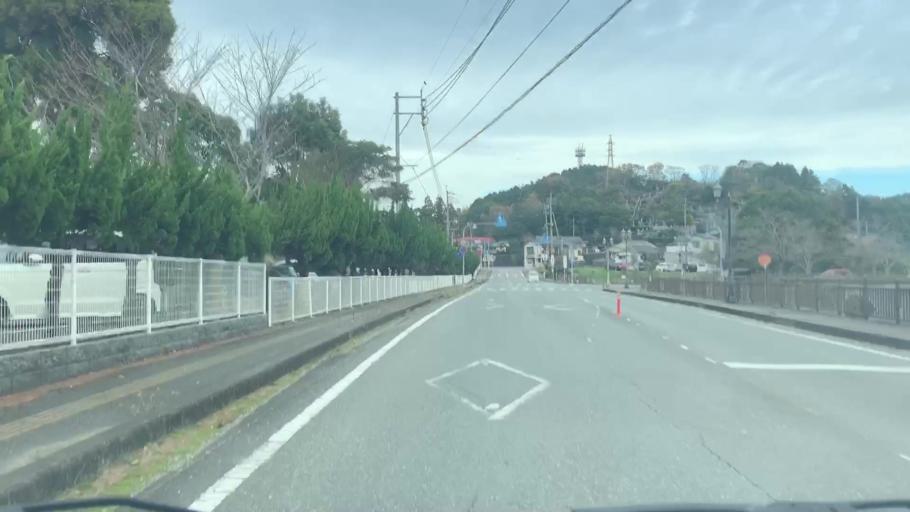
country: JP
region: Saga Prefecture
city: Ureshinomachi-shimojuku
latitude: 33.0984
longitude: 129.9802
